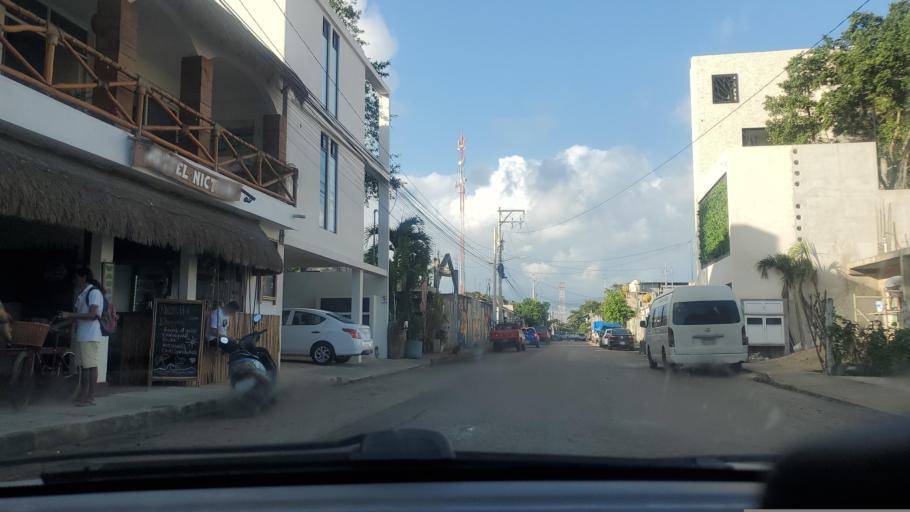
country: MX
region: Quintana Roo
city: Tulum
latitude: 20.2116
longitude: -87.4568
